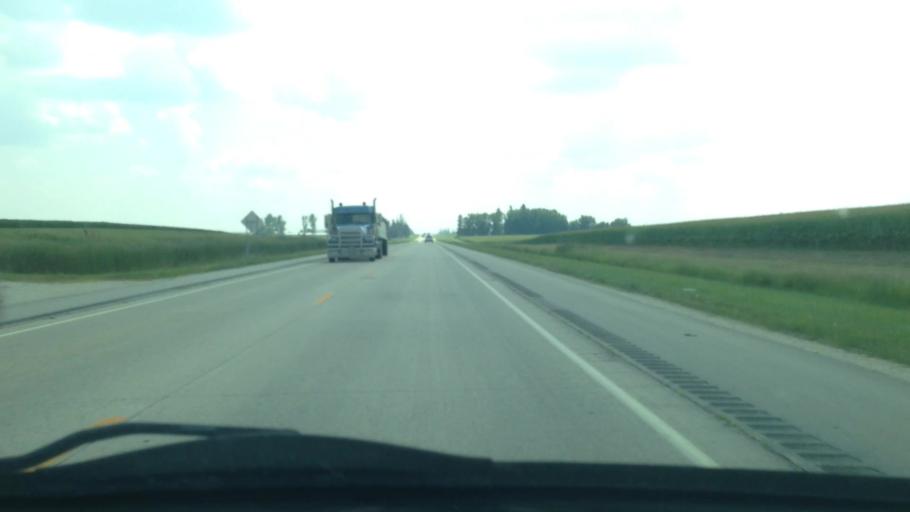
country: US
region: Minnesota
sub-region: Fillmore County
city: Spring Valley
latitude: 43.6709
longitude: -92.3896
